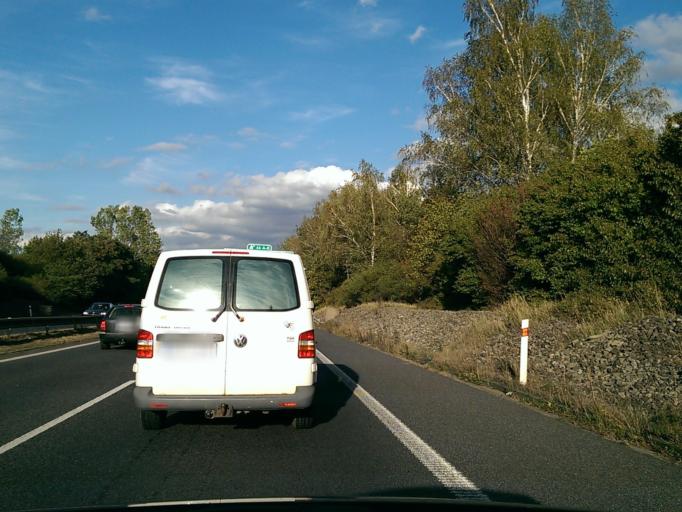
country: CZ
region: Central Bohemia
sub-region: Okres Mlada Boleslav
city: Mlada Boleslav
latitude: 50.4029
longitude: 14.9269
